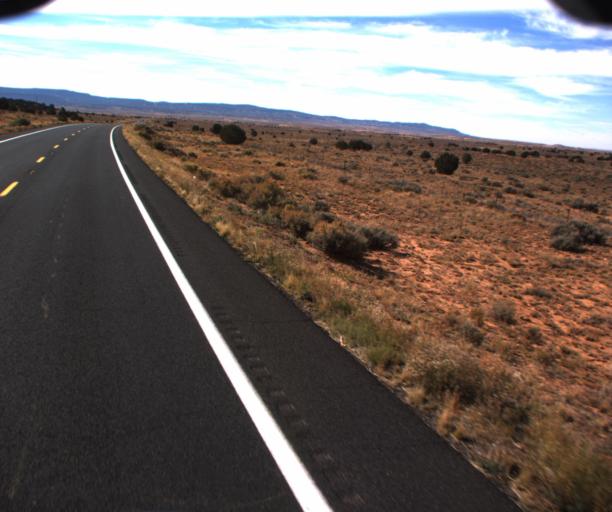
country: US
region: Arizona
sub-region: Coconino County
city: Kaibito
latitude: 36.5286
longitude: -110.7014
